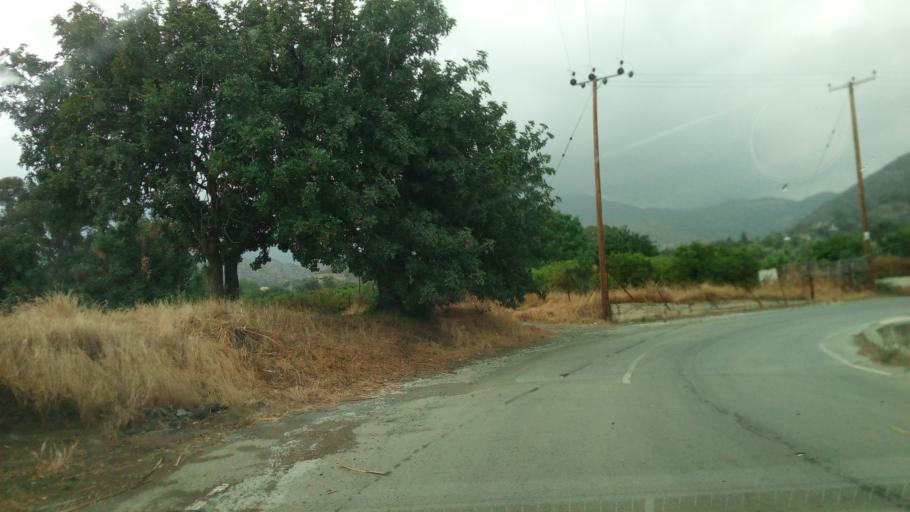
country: CY
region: Limassol
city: Pyrgos
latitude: 34.8567
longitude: 33.1936
